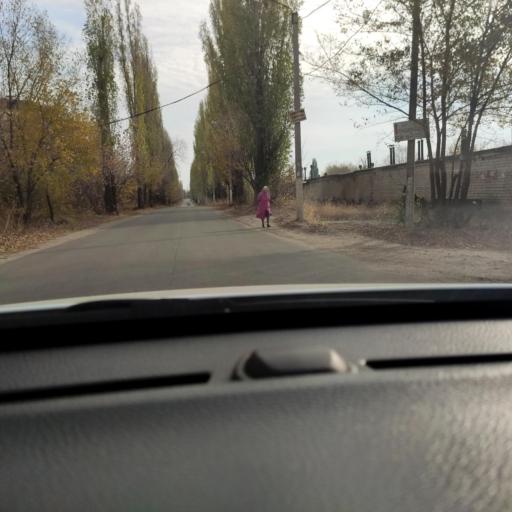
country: RU
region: Voronezj
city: Novaya Usman'
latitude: 51.6452
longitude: 39.3043
